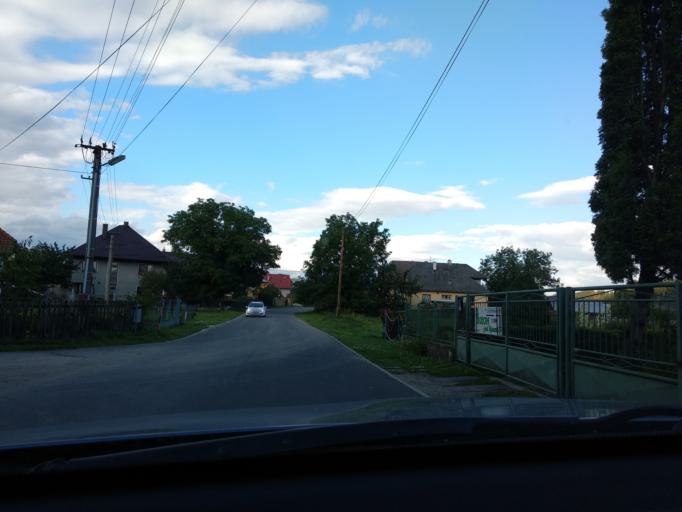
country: SK
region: Zilinsky
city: Ruzomberok
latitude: 49.0921
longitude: 19.4045
